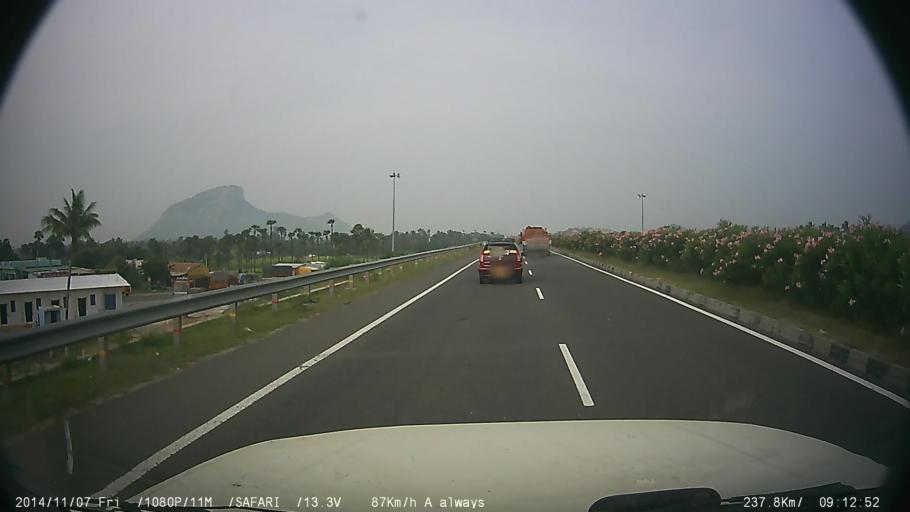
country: IN
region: Tamil Nadu
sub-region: Salem
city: Konganapuram
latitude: 11.4929
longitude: 77.8884
